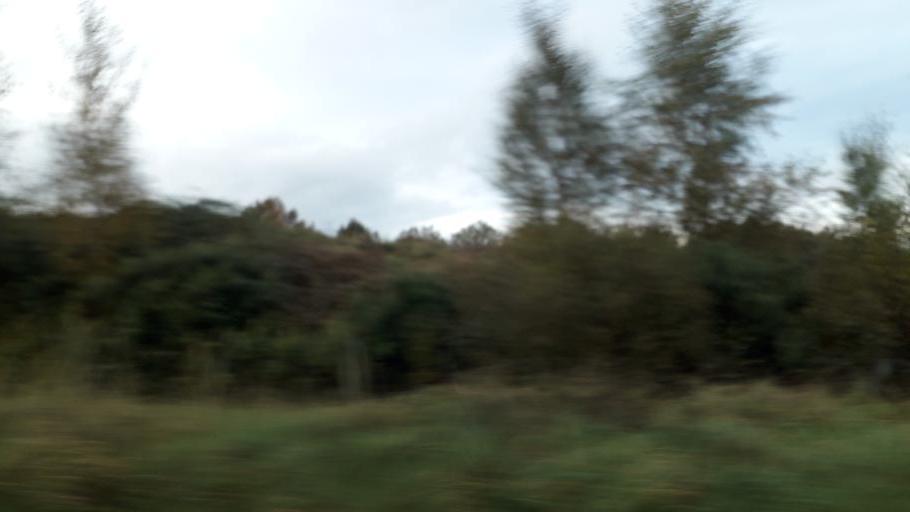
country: IE
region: Leinster
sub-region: An Longfort
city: Lanesborough
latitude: 53.7584
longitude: -7.9833
